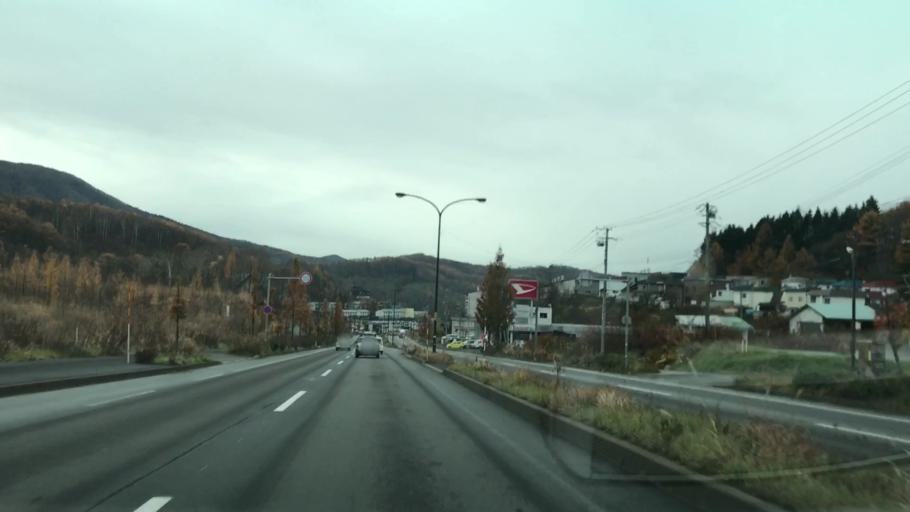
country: JP
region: Hokkaido
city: Otaru
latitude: 43.2134
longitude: 140.9382
